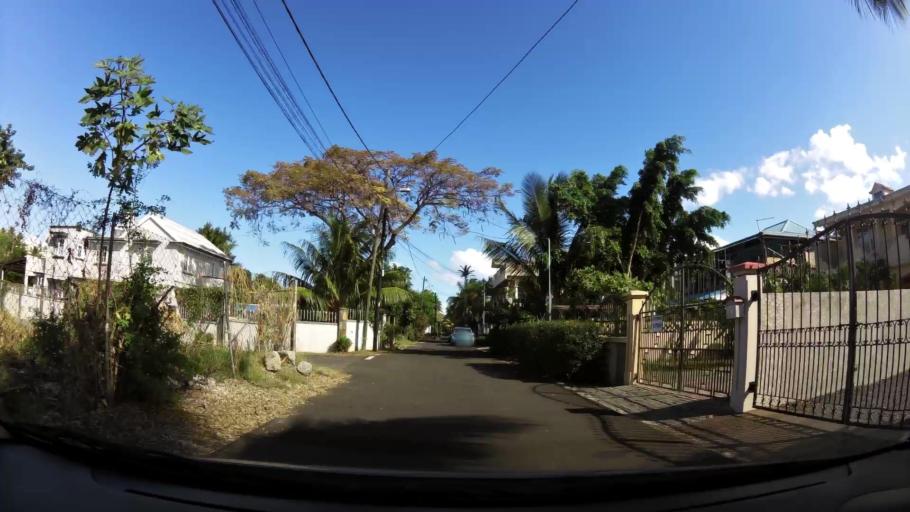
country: MU
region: Black River
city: Albion
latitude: -20.2142
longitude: 57.4055
